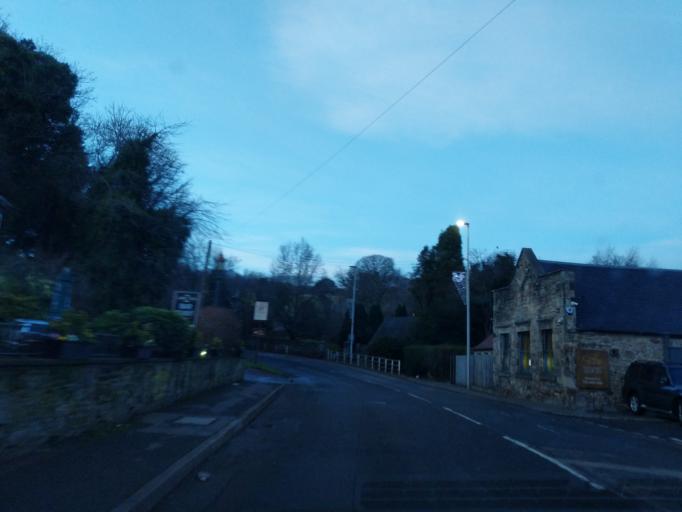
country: GB
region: Scotland
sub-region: Midlothian
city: Bonnyrigg
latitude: 55.8836
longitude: -3.1153
